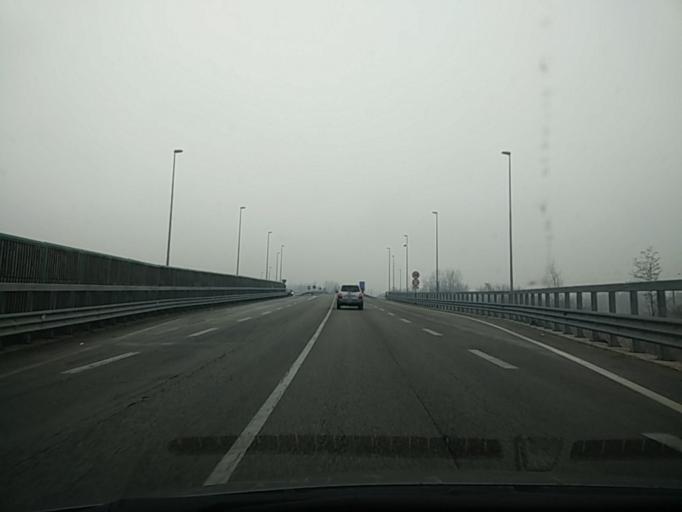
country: IT
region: Veneto
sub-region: Provincia di Belluno
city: Seren del Grappa
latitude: 46.0071
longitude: 11.8721
